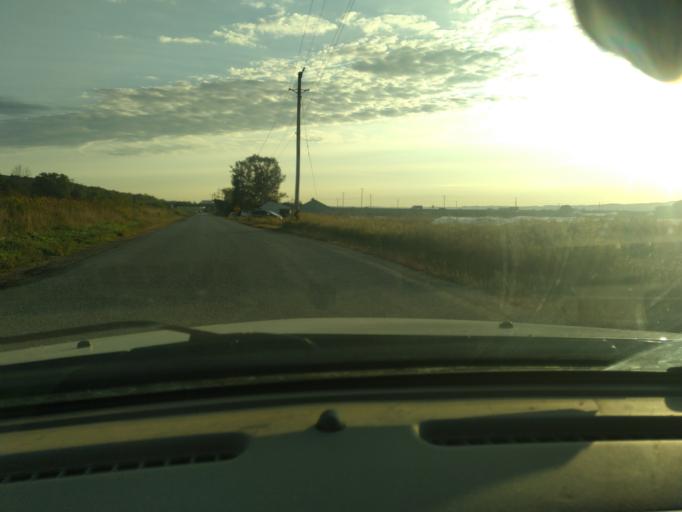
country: CA
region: Ontario
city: Bradford West Gwillimbury
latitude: 44.0500
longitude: -79.6138
